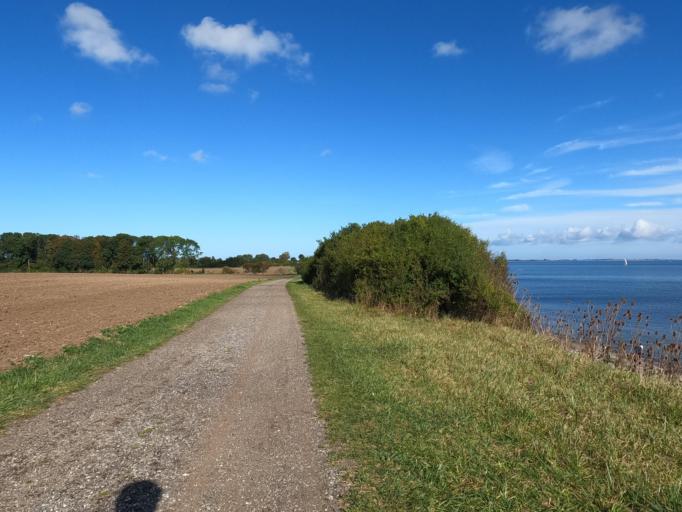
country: DE
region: Schleswig-Holstein
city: Neukirchen
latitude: 54.3159
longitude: 11.0739
